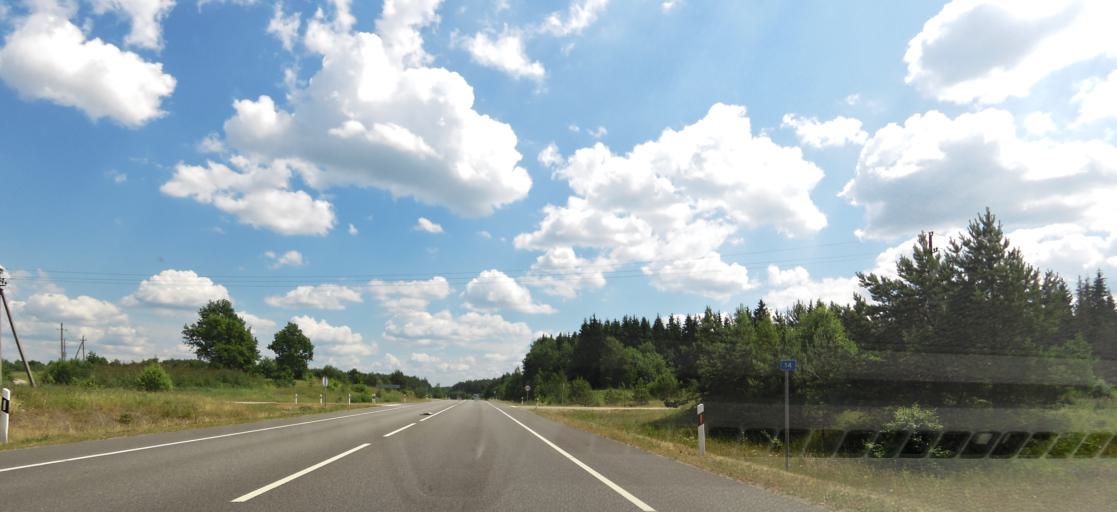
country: LT
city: Skaidiskes
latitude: 54.6165
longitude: 25.4213
